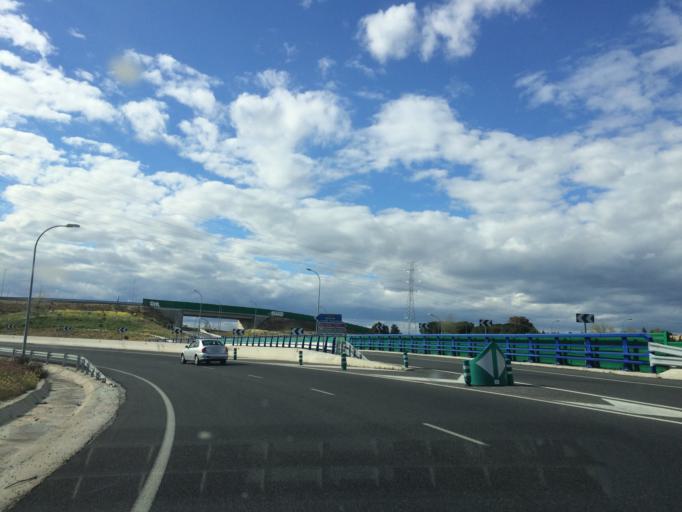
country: ES
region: Madrid
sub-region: Provincia de Madrid
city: Pozuelo de Alarcon
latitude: 40.3976
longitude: -3.8300
